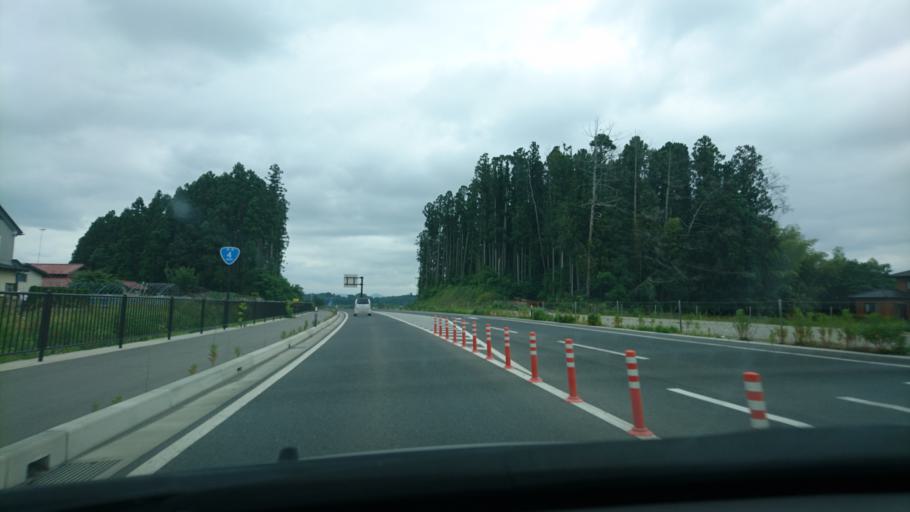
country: JP
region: Miyagi
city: Furukawa
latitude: 38.7427
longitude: 141.0388
